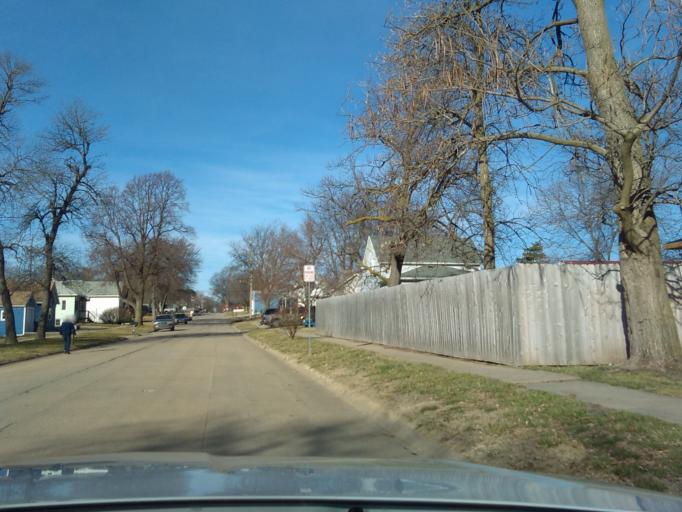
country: US
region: Nebraska
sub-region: Seward County
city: Milford
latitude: 40.7732
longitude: -97.0474
